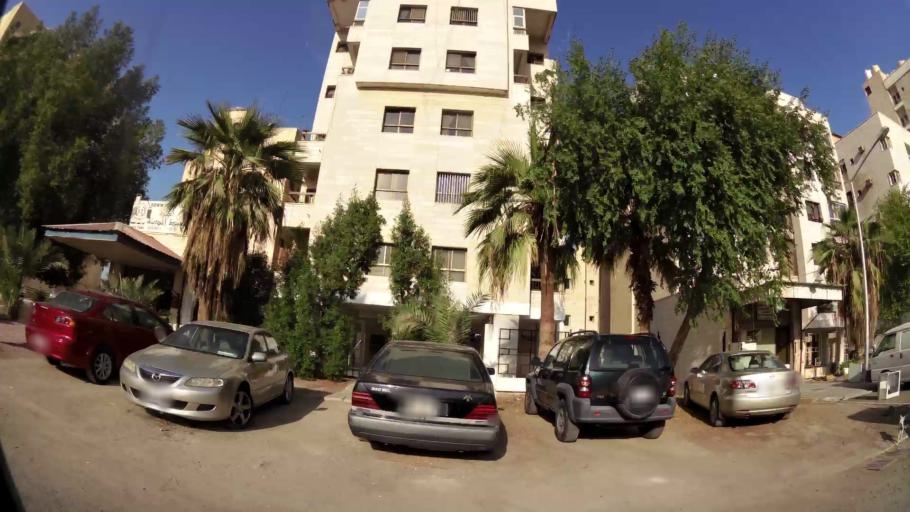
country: KW
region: Muhafazat Hawalli
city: As Salimiyah
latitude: 29.3360
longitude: 48.0834
